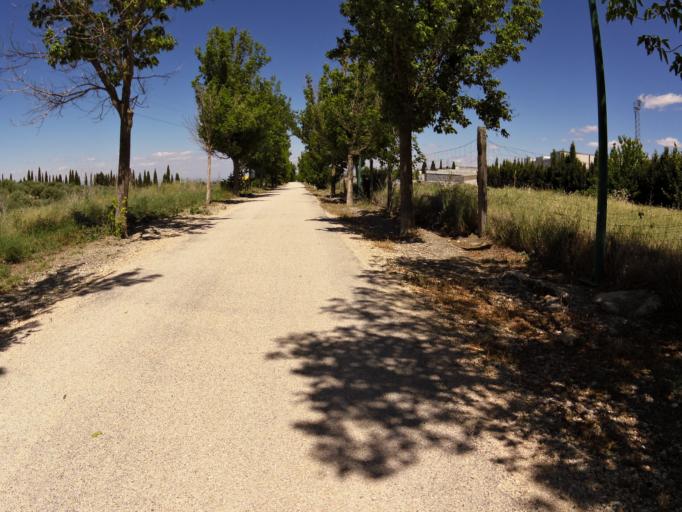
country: ES
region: Andalusia
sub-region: Provincia de Jaen
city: Torre del Campo
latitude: 37.7756
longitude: -3.9014
